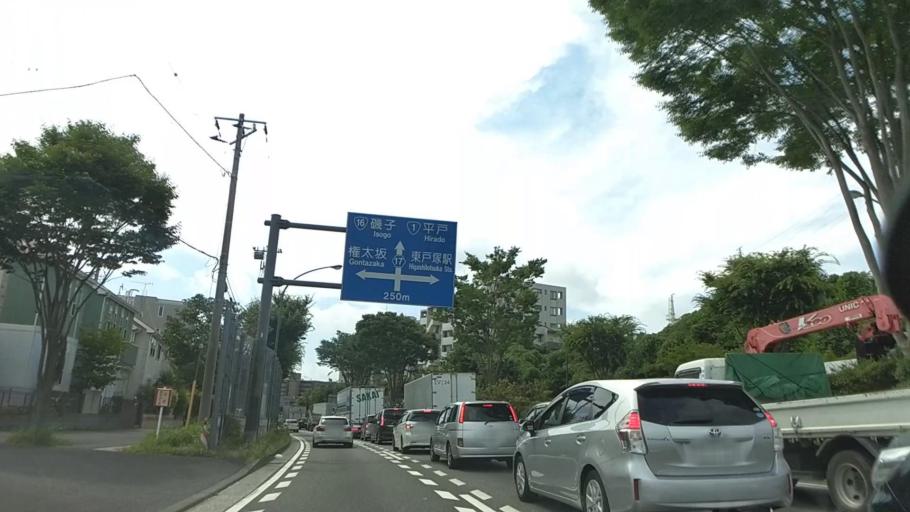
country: JP
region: Kanagawa
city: Yokohama
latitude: 35.4376
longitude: 139.5610
